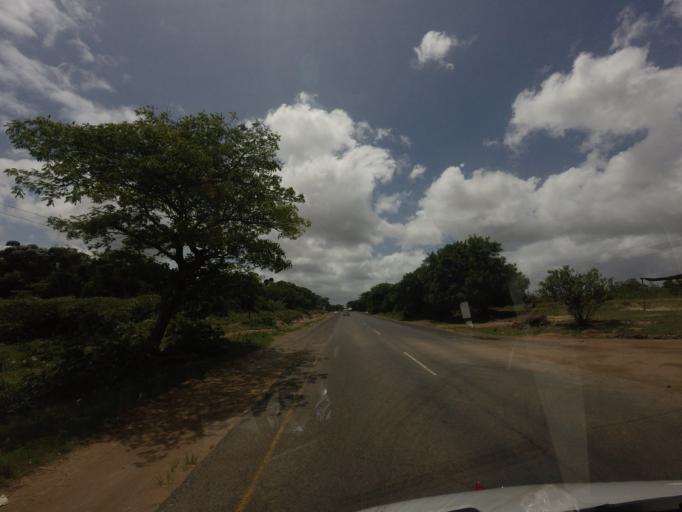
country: ZA
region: KwaZulu-Natal
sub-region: uMkhanyakude District Municipality
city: Mtubatuba
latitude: -28.3801
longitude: 32.3633
